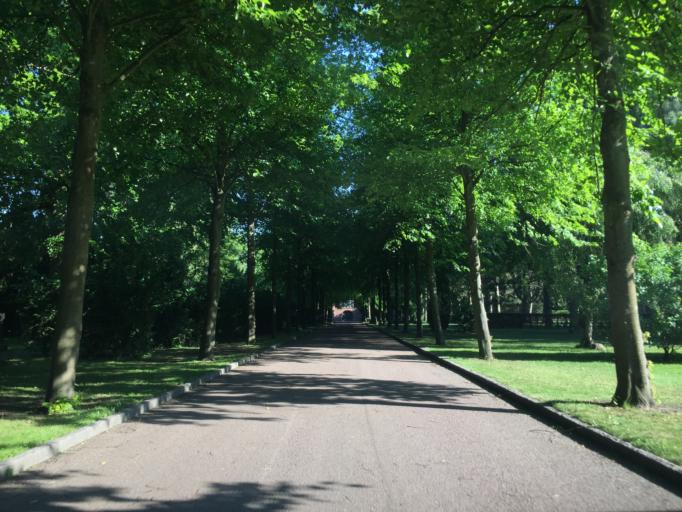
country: DK
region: Capital Region
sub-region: Frederiksberg Kommune
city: Frederiksberg
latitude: 55.6559
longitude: 12.5326
